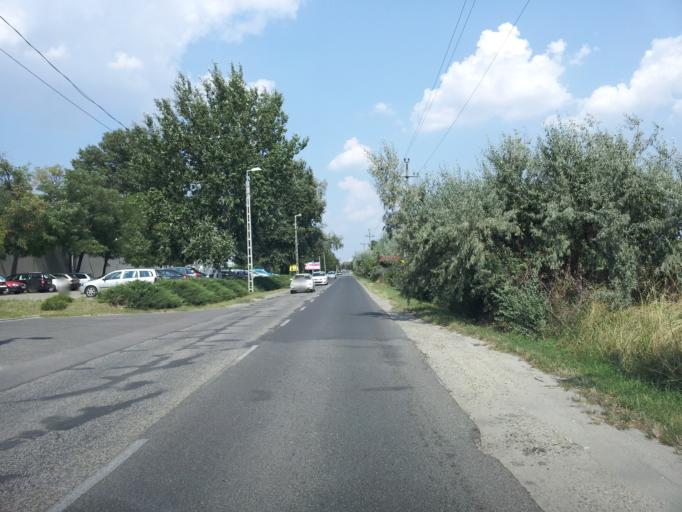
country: HU
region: Pest
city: Taksony
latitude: 47.3260
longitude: 19.0551
